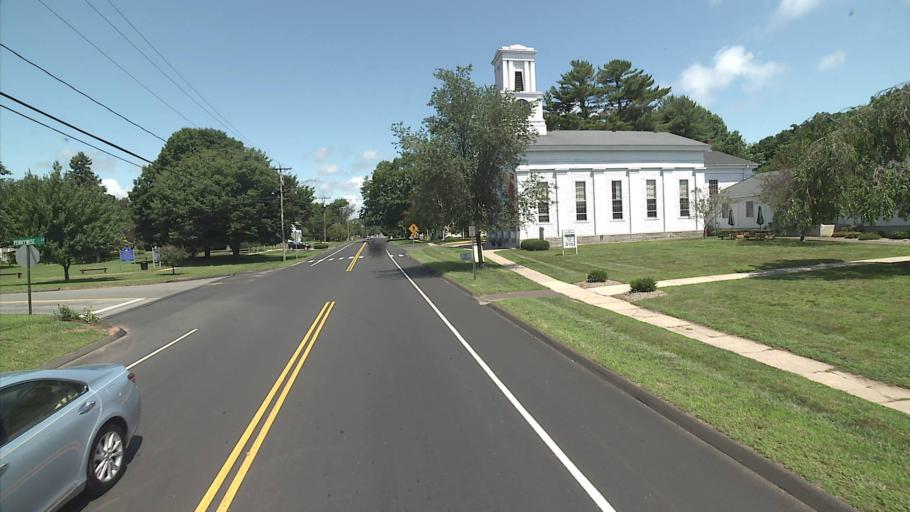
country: US
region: Connecticut
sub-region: Middlesex County
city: Old Saybrook
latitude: 41.2863
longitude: -72.3753
